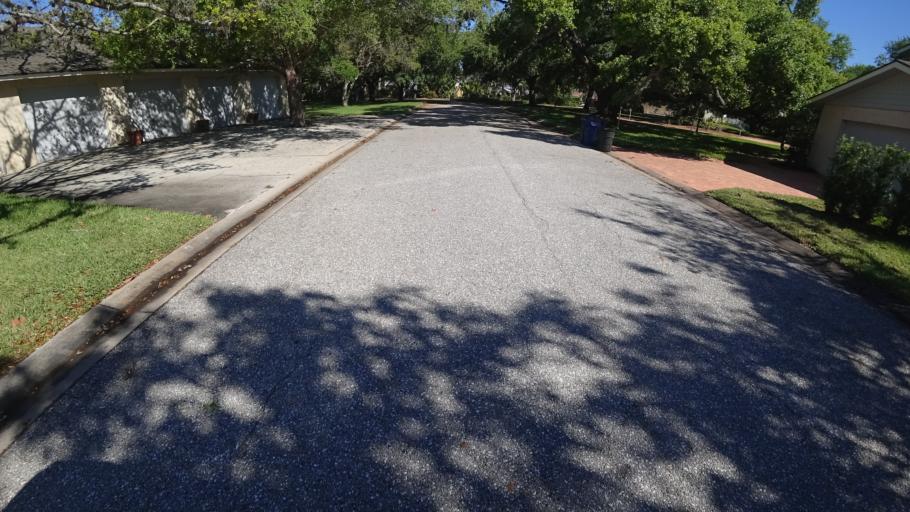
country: US
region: Florida
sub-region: Manatee County
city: West Bradenton
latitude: 27.4846
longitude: -82.6419
